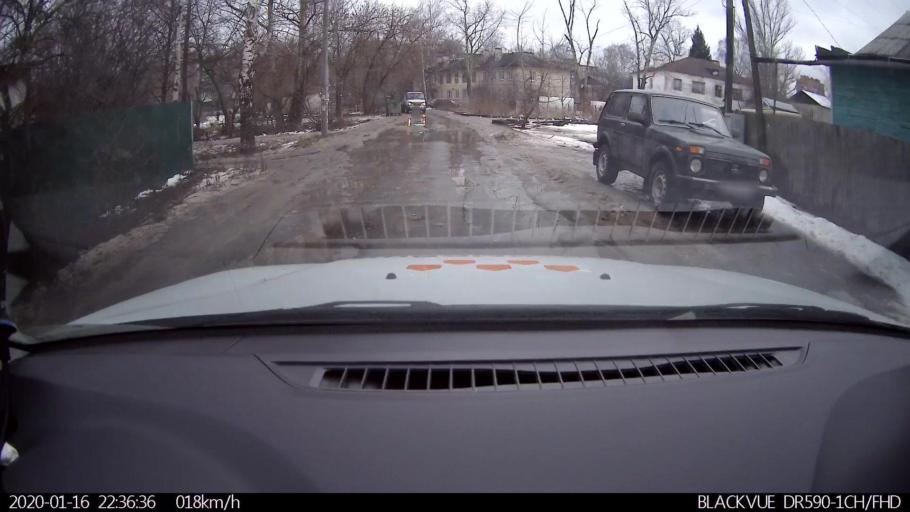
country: RU
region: Nizjnij Novgorod
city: Nizhniy Novgorod
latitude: 56.2778
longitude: 43.9086
